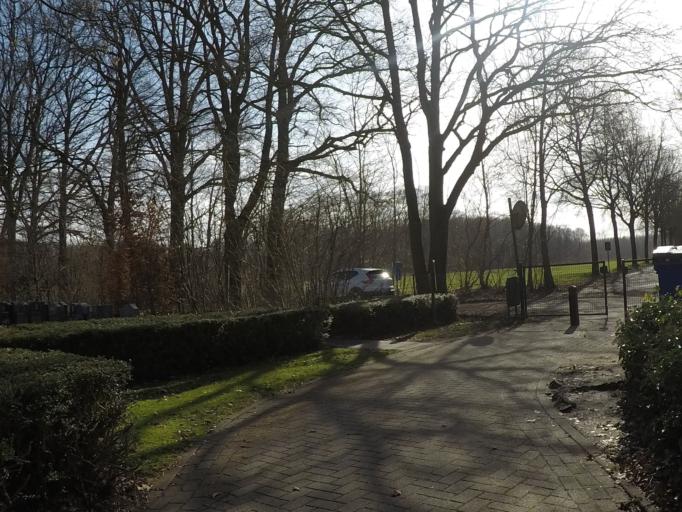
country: BE
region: Flanders
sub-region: Provincie Antwerpen
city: Ranst
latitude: 51.2028
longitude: 4.5619
